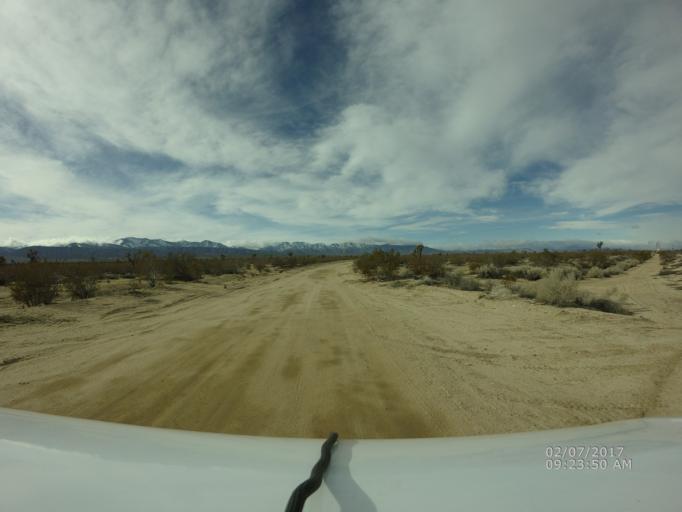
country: US
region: California
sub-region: Los Angeles County
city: Lake Los Angeles
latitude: 34.5168
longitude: -117.7437
